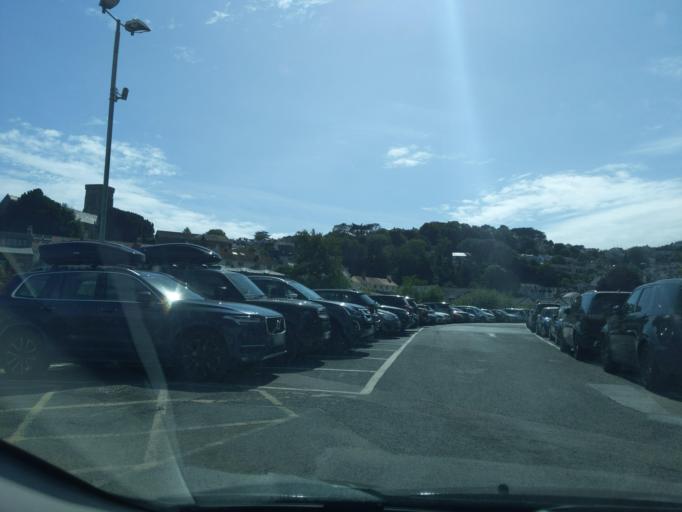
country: GB
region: England
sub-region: Devon
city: Salcombe
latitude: 50.2409
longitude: -3.7681
